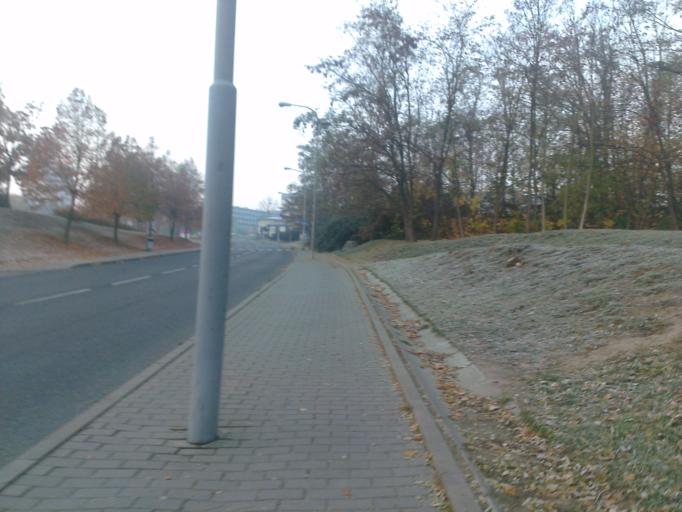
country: CZ
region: South Moravian
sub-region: Mesto Brno
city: Mokra Hora
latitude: 49.2294
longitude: 16.5770
